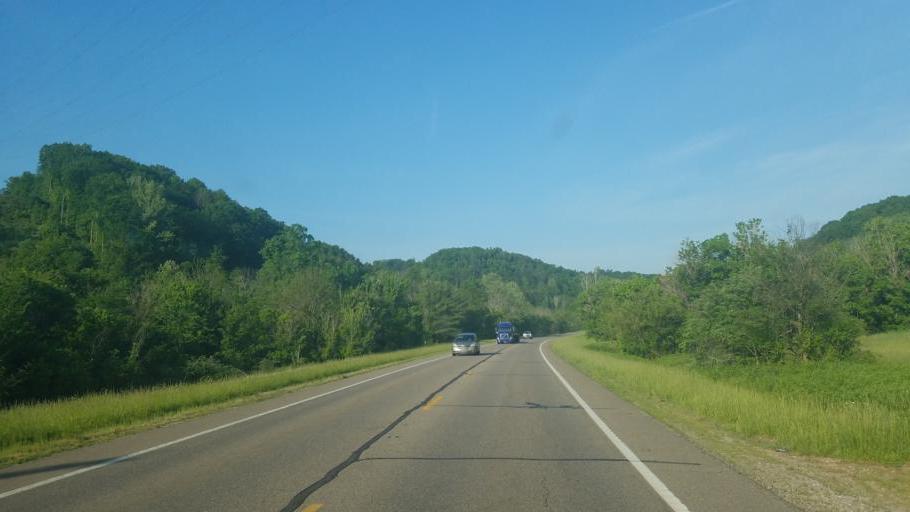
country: US
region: West Virginia
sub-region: Mason County
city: New Haven
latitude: 39.1175
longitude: -81.8901
